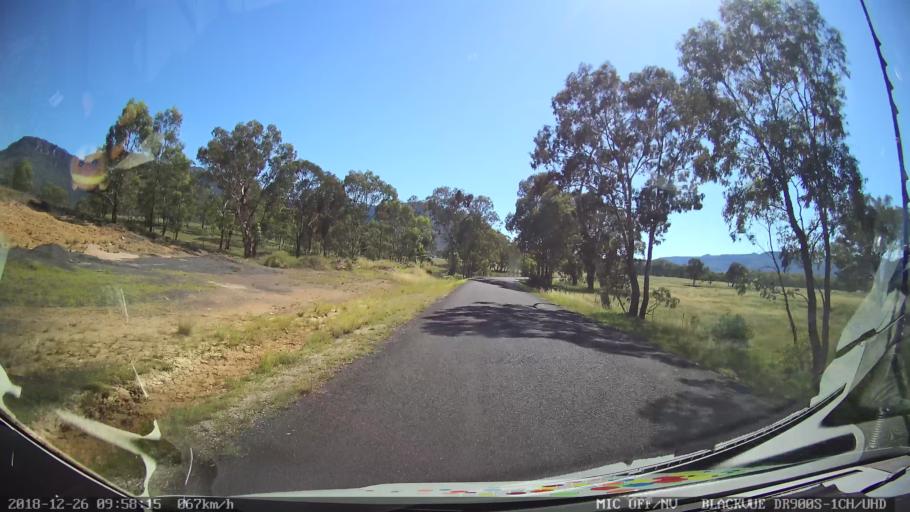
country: AU
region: New South Wales
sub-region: Mid-Western Regional
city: Kandos
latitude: -33.0389
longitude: 150.2027
